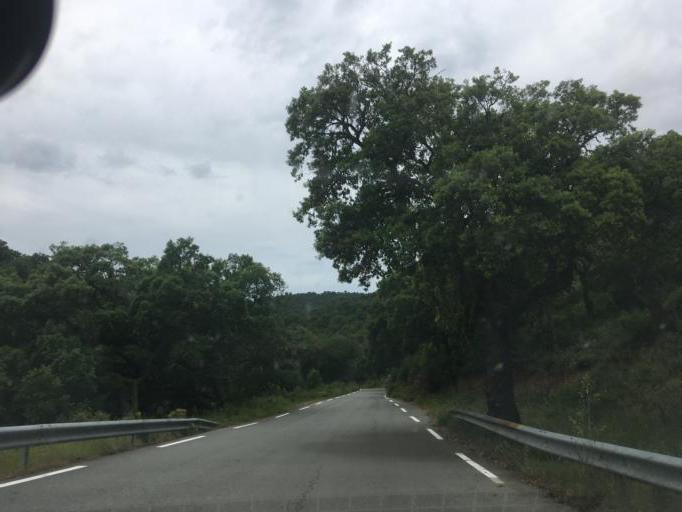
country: FR
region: Provence-Alpes-Cote d'Azur
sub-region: Departement du Var
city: Pierrefeu-du-Var
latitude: 43.2126
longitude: 6.2189
